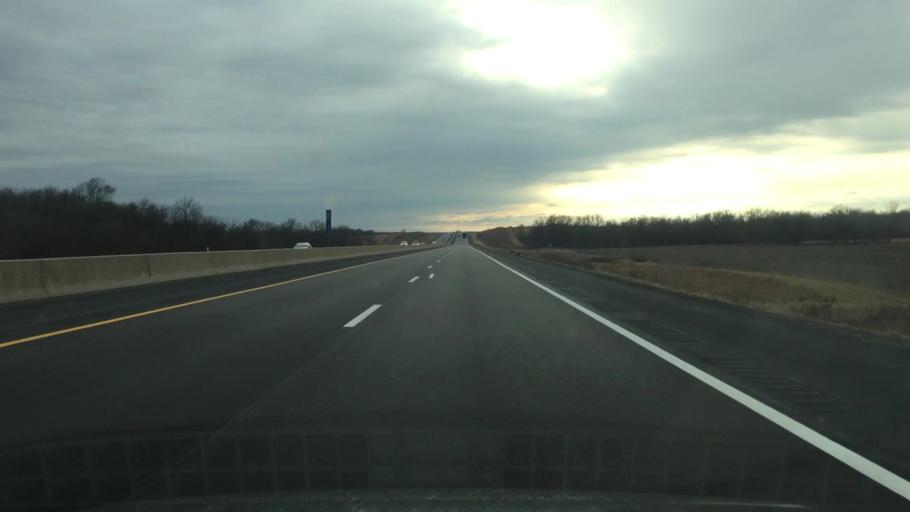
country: US
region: Kansas
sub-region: Lyon County
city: Emporia
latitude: 38.5896
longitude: -96.0801
